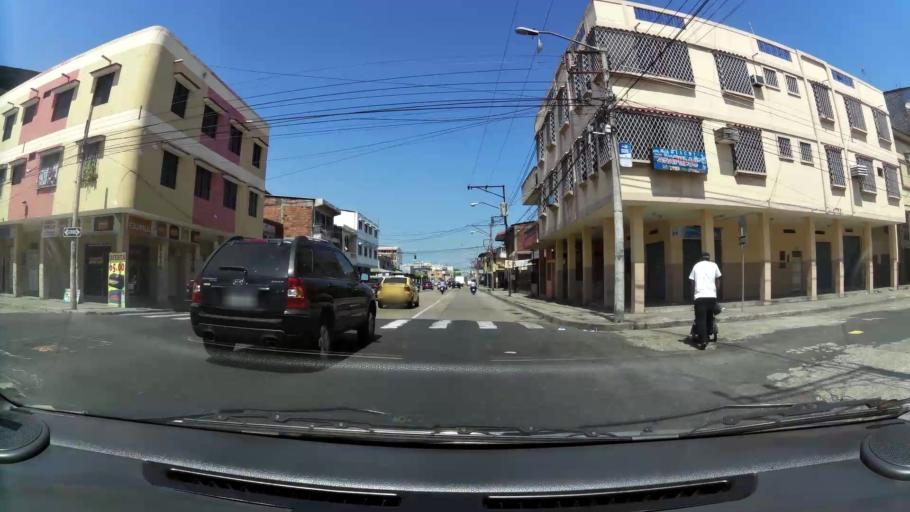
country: EC
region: Guayas
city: Guayaquil
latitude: -2.2036
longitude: -79.8952
